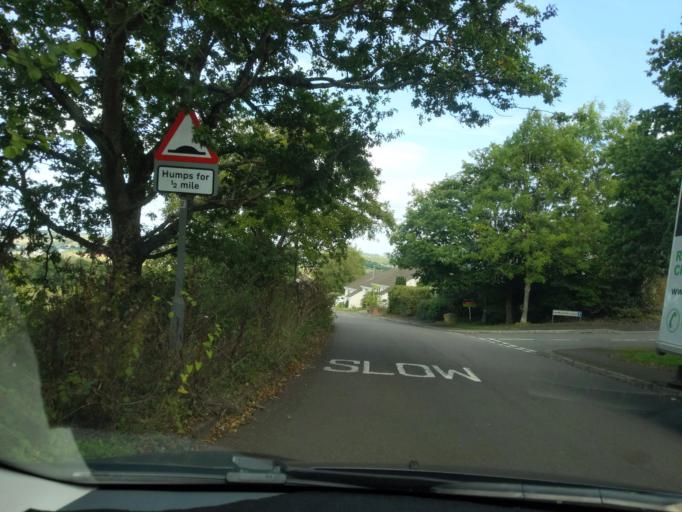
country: GB
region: England
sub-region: Devon
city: Kingskerswell
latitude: 50.4777
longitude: -3.5737
